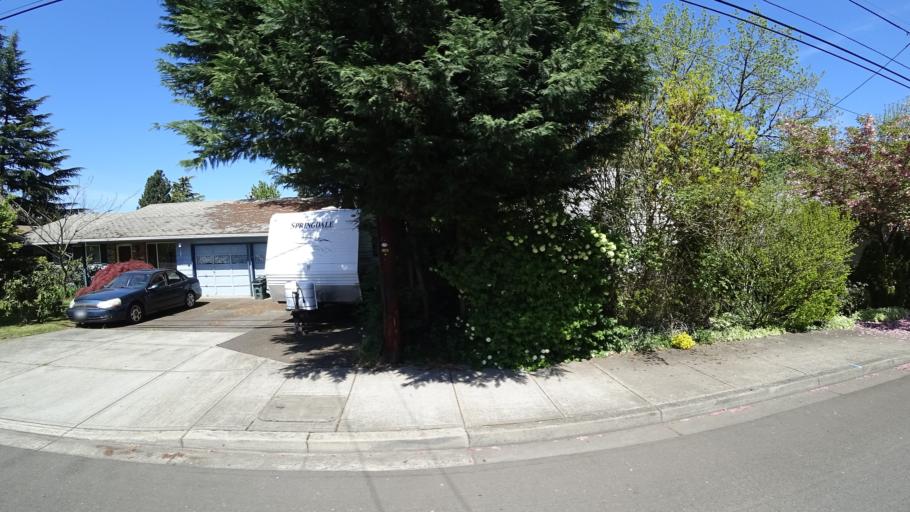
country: US
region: Oregon
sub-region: Washington County
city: Hillsboro
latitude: 45.5187
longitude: -122.9642
